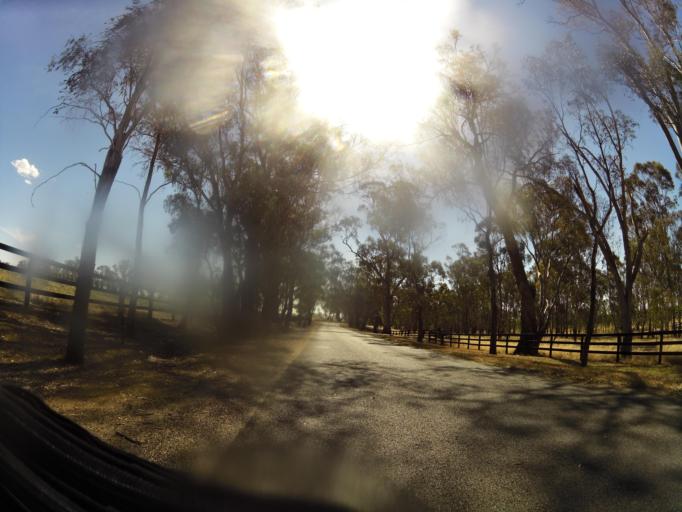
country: AU
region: Victoria
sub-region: Campaspe
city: Kyabram
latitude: -36.8596
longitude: 145.0903
